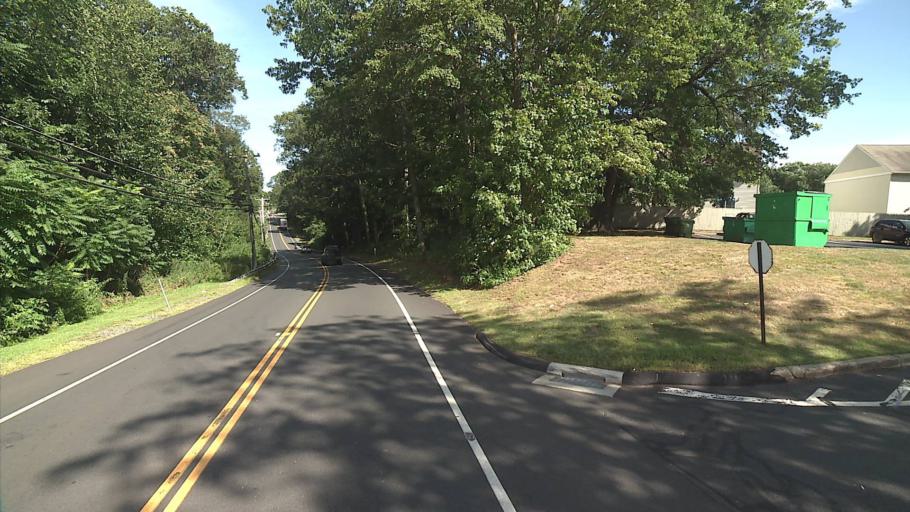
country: US
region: Connecticut
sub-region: New Haven County
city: Cheshire
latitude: 41.4984
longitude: -72.8990
